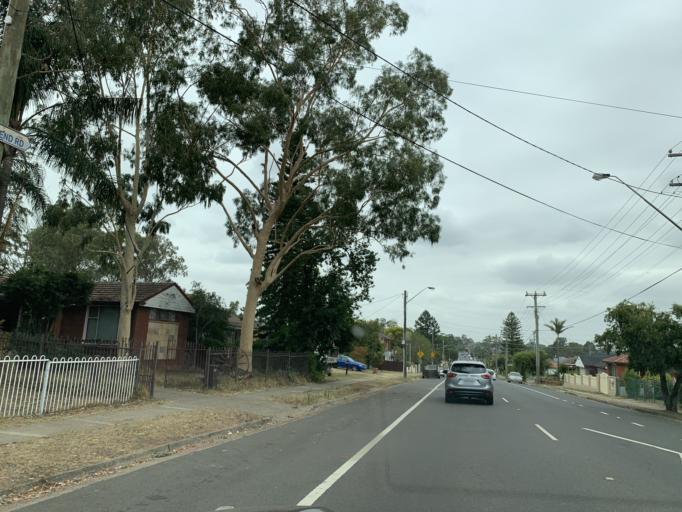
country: AU
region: New South Wales
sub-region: Blacktown
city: Doonside
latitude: -33.7569
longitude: 150.8707
